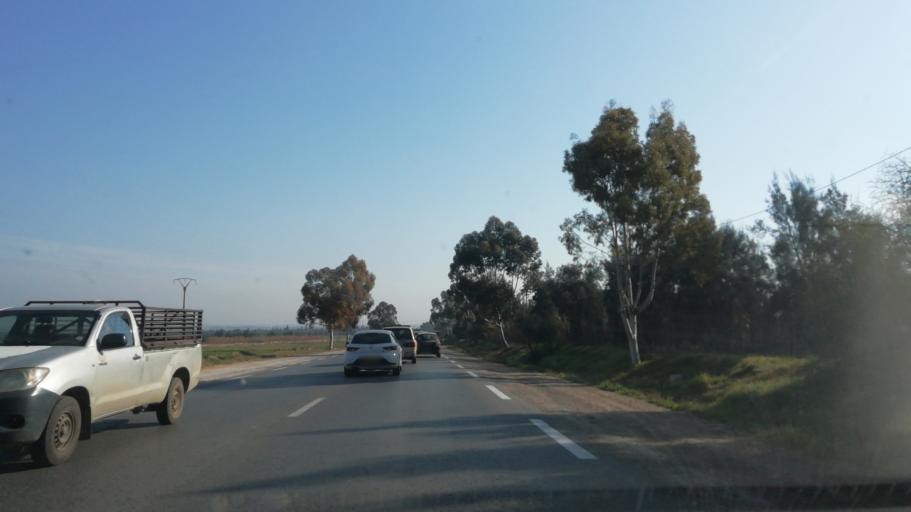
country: DZ
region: Relizane
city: Relizane
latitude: 35.7282
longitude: 0.4071
